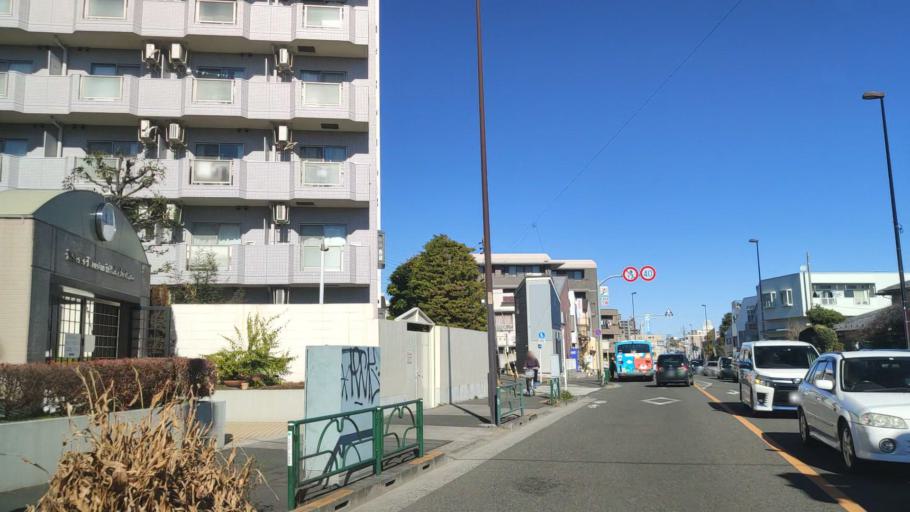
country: JP
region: Tokyo
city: Mitaka-shi
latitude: 35.6746
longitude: 139.5670
